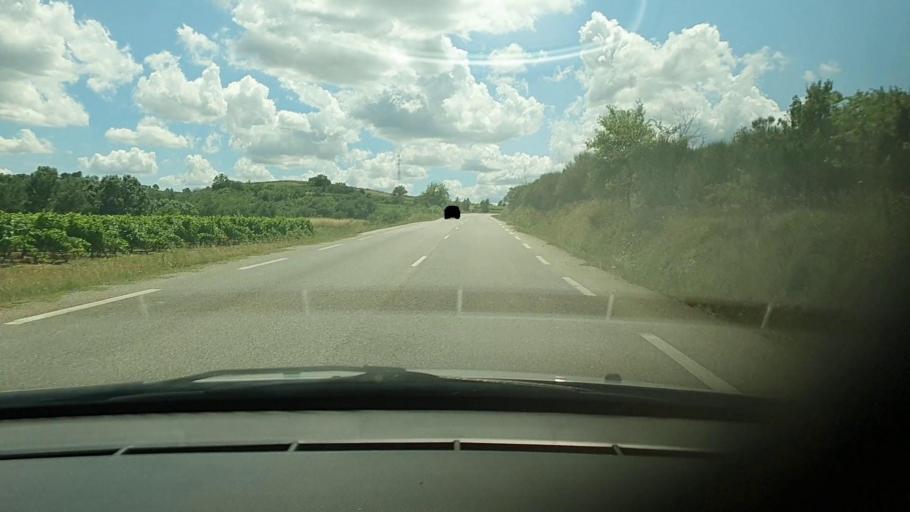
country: FR
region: Languedoc-Roussillon
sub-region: Departement du Gard
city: Mons
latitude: 44.0631
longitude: 4.2234
